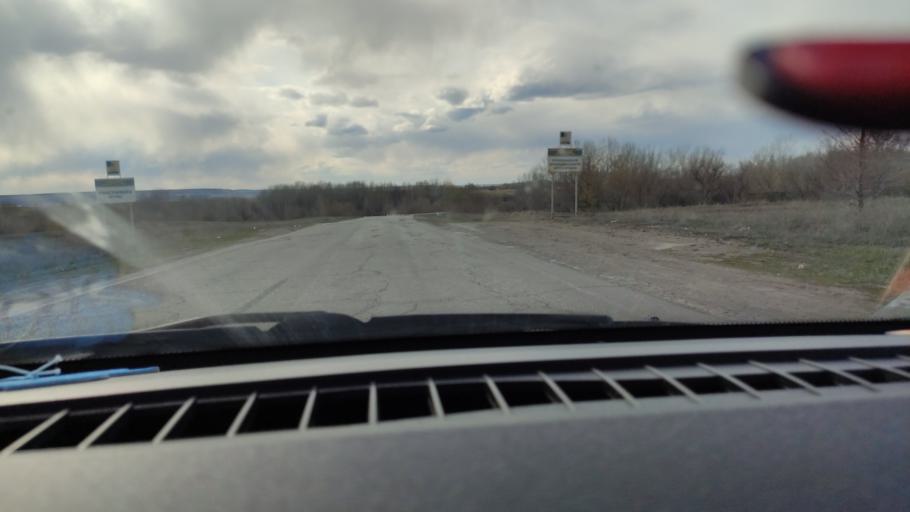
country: RU
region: Saratov
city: Rovnoye
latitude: 51.0479
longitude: 46.0487
